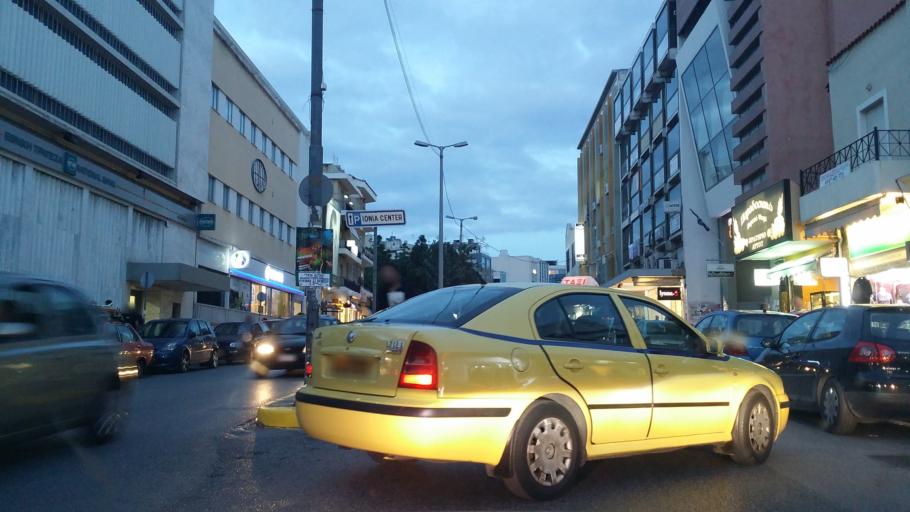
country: GR
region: Attica
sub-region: Nomarchia Athinas
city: Nea Ionia
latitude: 38.0427
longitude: 23.7535
